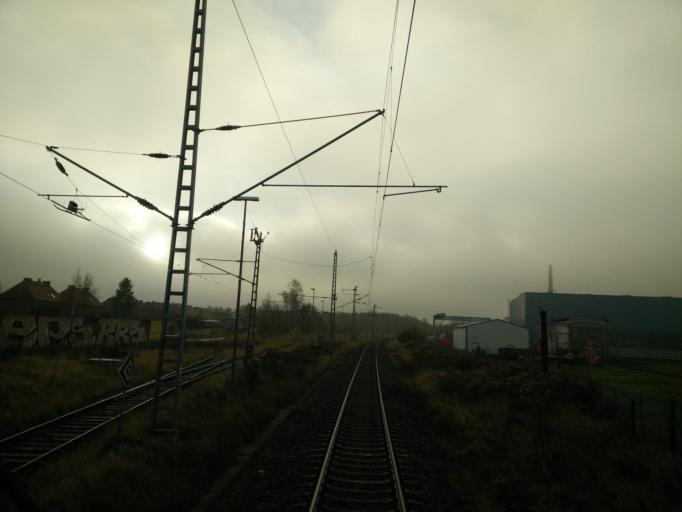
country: DE
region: Mecklenburg-Vorpommern
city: Wismar
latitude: 53.8912
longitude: 11.4749
